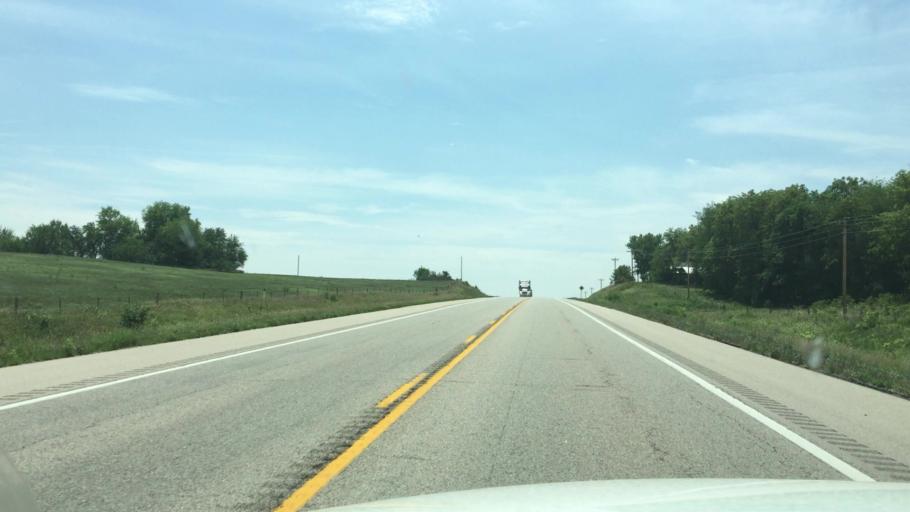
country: US
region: Kansas
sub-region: Jackson County
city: Holton
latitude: 39.6267
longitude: -95.7311
